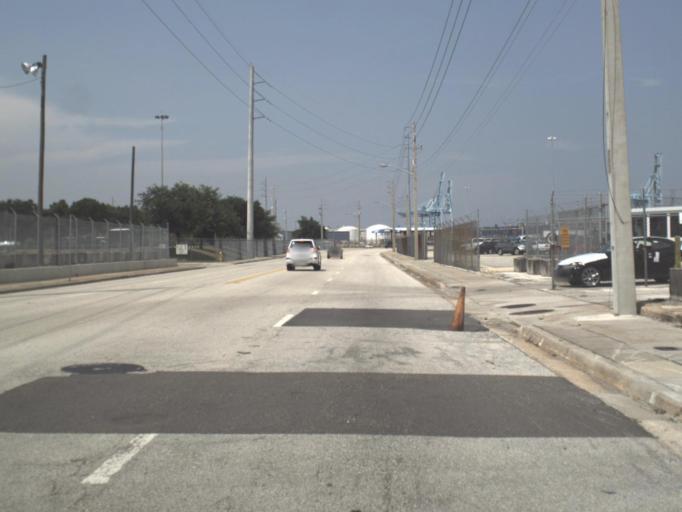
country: US
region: Florida
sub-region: Duval County
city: Jacksonville
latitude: 30.3460
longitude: -81.6277
